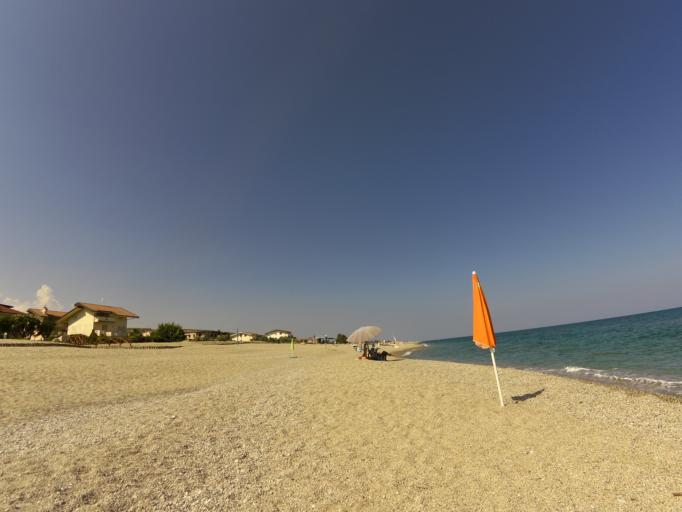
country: IT
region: Calabria
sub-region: Provincia di Reggio Calabria
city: Riace Marina
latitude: 38.3985
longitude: 16.5418
